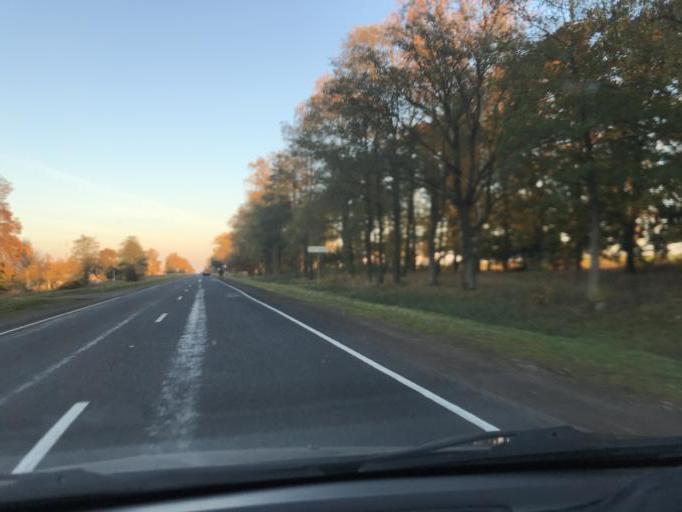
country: BY
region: Minsk
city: Staryya Darohi
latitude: 53.0578
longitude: 28.4540
